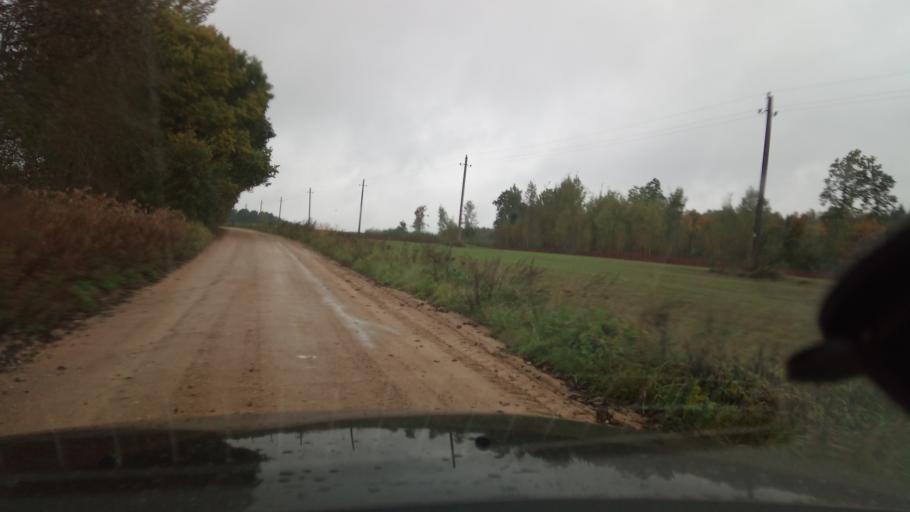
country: LT
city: Skaidiskes
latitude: 54.5552
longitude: 25.4858
